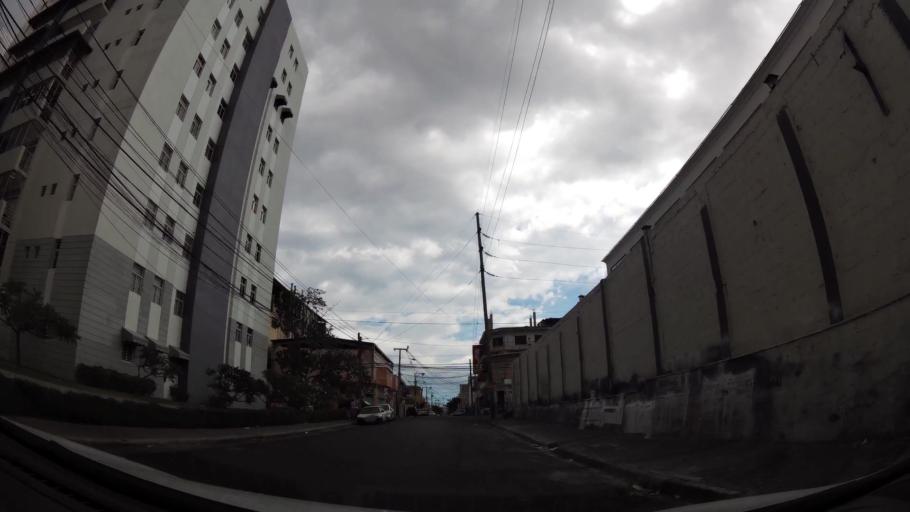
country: DO
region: Nacional
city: San Carlos
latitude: 18.4896
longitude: -69.9169
